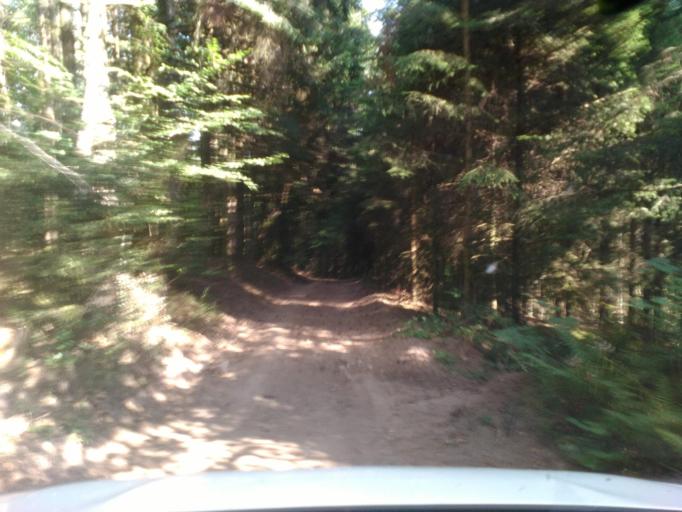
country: FR
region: Lorraine
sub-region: Departement des Vosges
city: Senones
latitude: 48.3627
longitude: 6.9942
